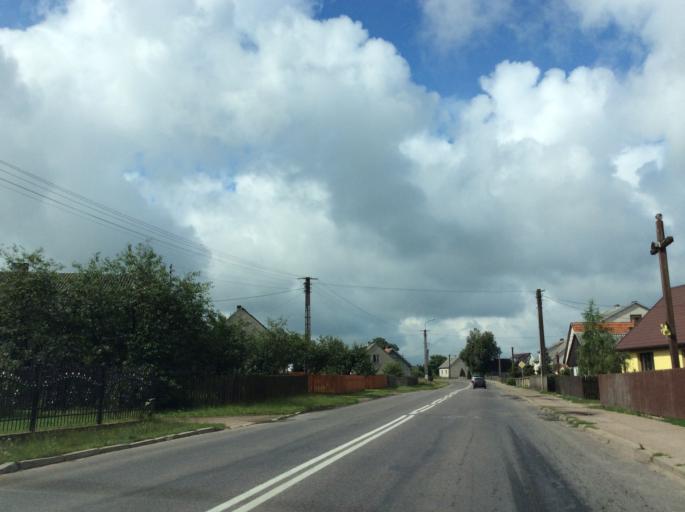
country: PL
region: Warmian-Masurian Voivodeship
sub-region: Powiat szczycienski
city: Rozogi
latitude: 53.4355
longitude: 21.3671
